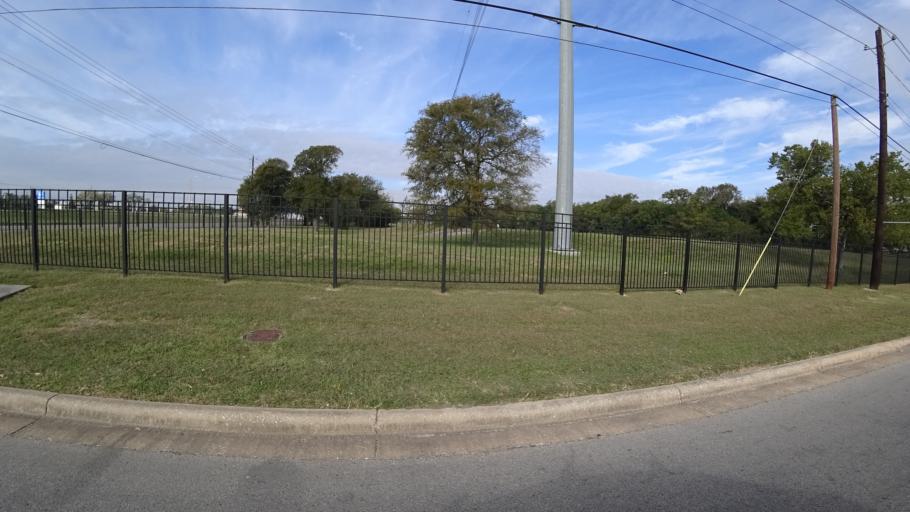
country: US
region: Texas
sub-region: Travis County
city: Austin
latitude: 30.2141
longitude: -97.7204
